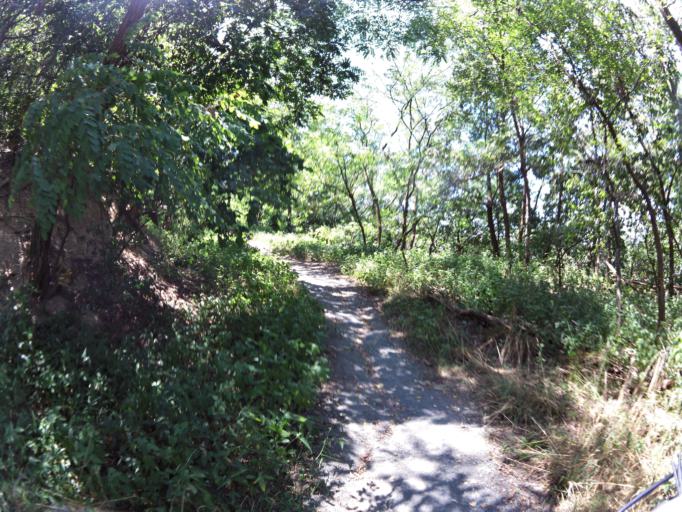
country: KR
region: Daegu
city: Daegu
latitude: 35.8517
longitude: 128.6470
